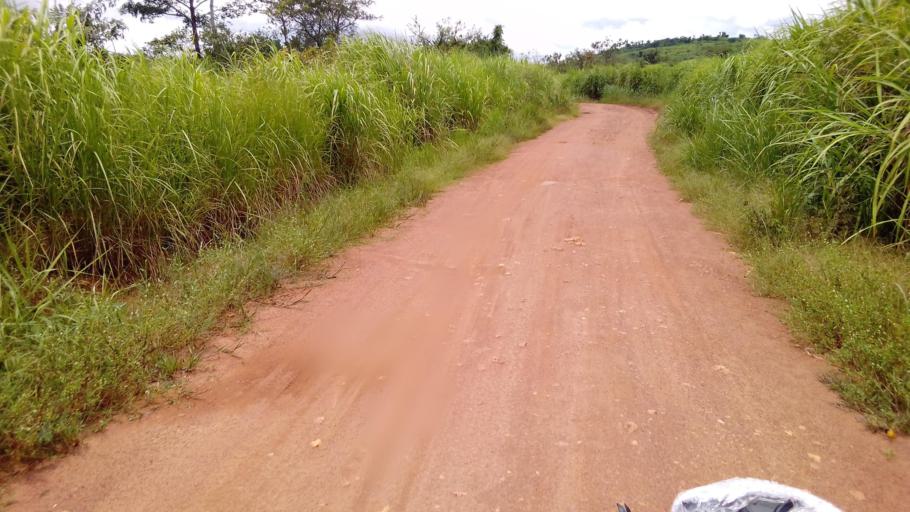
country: SL
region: Eastern Province
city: Koidu
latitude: 8.6763
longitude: -10.9358
